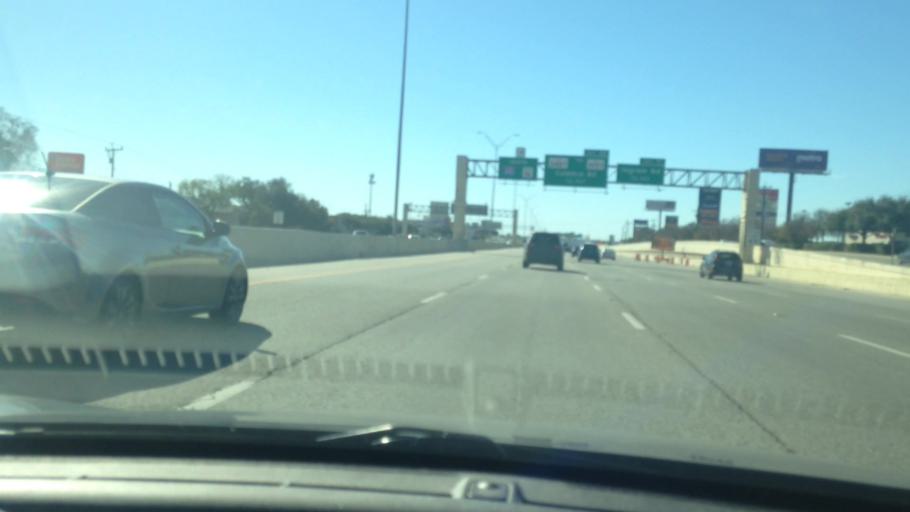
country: US
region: Texas
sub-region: Bexar County
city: Leon Valley
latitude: 29.4752
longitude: -98.6104
